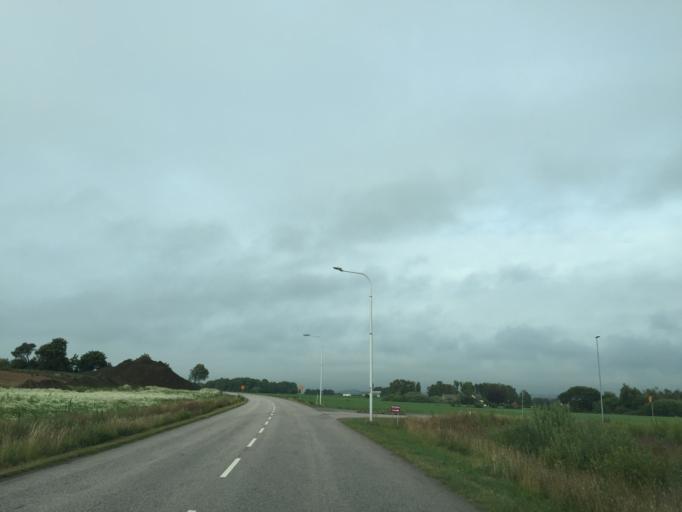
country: SE
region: Halland
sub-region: Falkenbergs Kommun
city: Falkenberg
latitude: 56.8750
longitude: 12.5553
